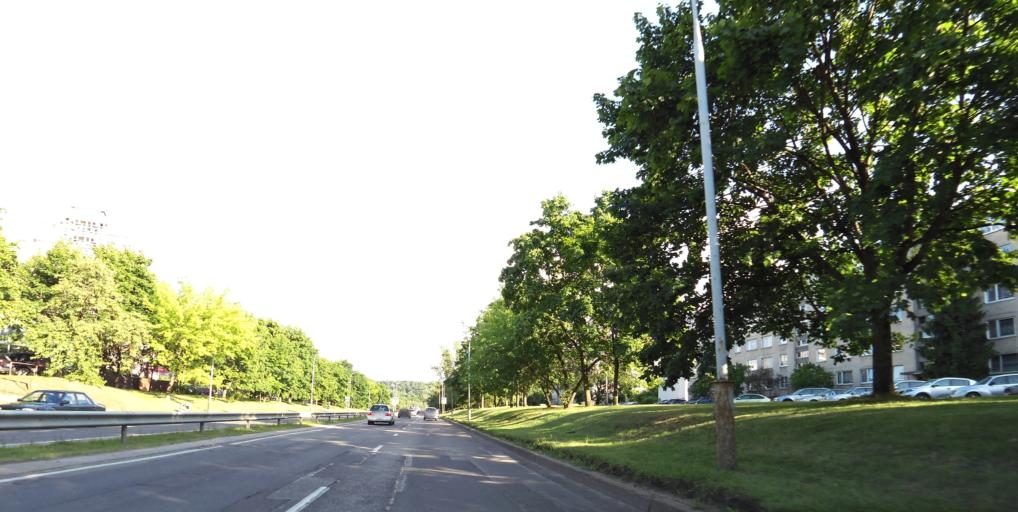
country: LT
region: Vilnius County
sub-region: Vilnius
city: Vilnius
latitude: 54.6997
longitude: 25.2935
